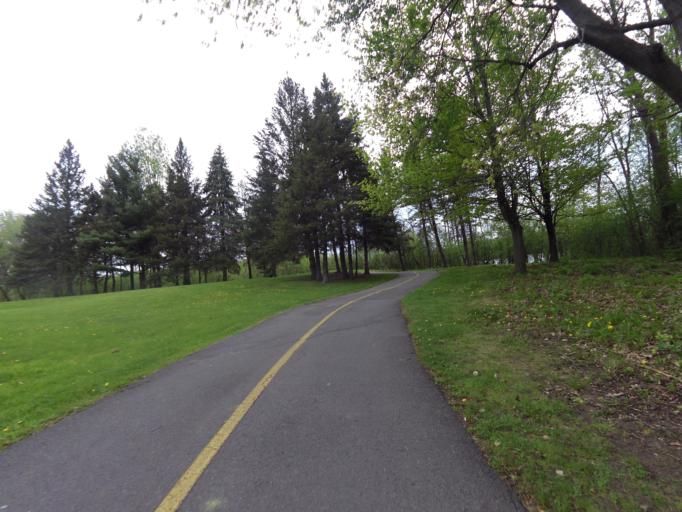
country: CA
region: Ontario
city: Ottawa
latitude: 45.4420
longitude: -75.7057
